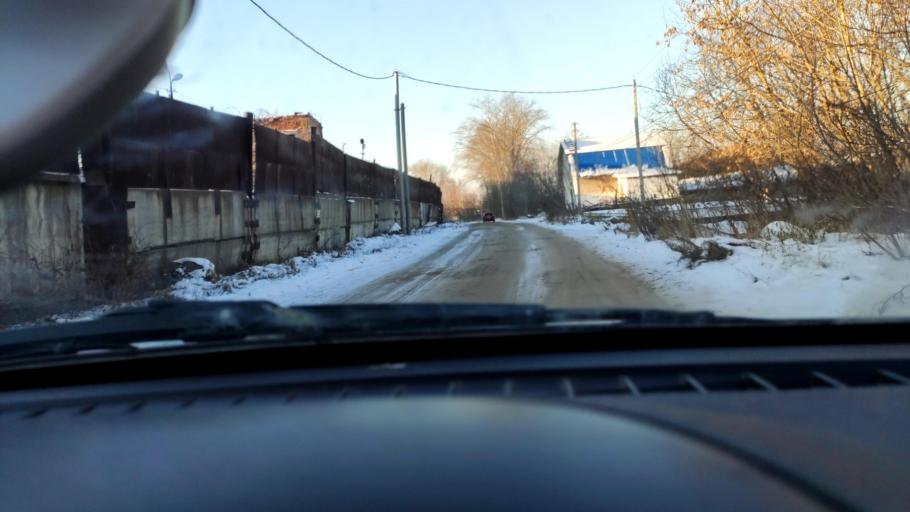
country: RU
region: Perm
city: Perm
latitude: 58.0718
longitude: 56.3593
